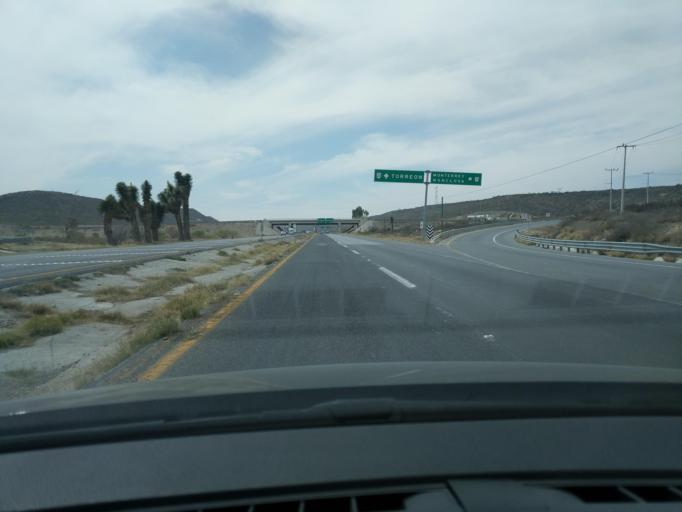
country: MX
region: Coahuila
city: Saltillo
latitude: 25.4535
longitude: -101.0615
